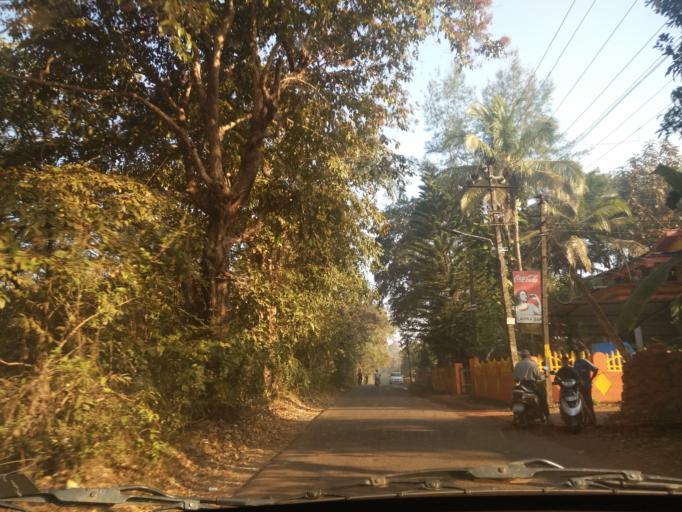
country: IN
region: Goa
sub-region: South Goa
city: Davorlim
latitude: 15.2807
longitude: 74.0063
